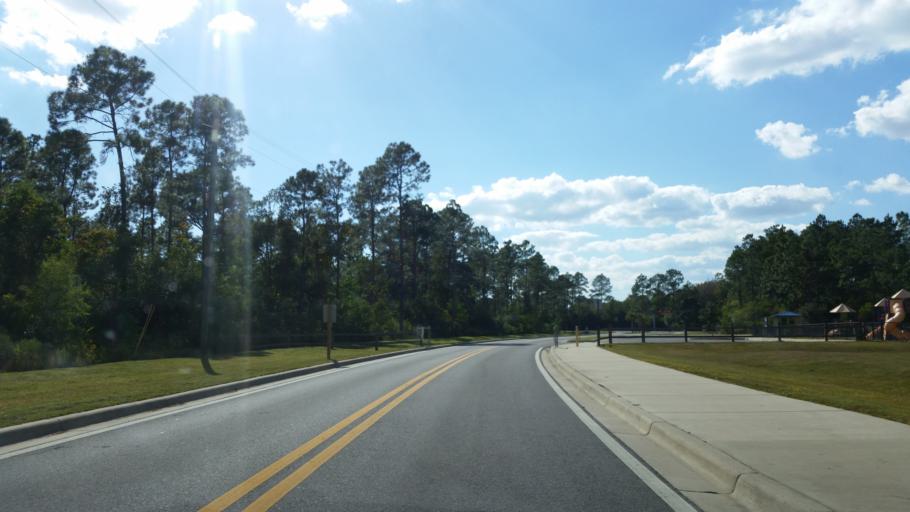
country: US
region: Florida
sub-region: Escambia County
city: Myrtle Grove
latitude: 30.3846
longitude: -87.3998
